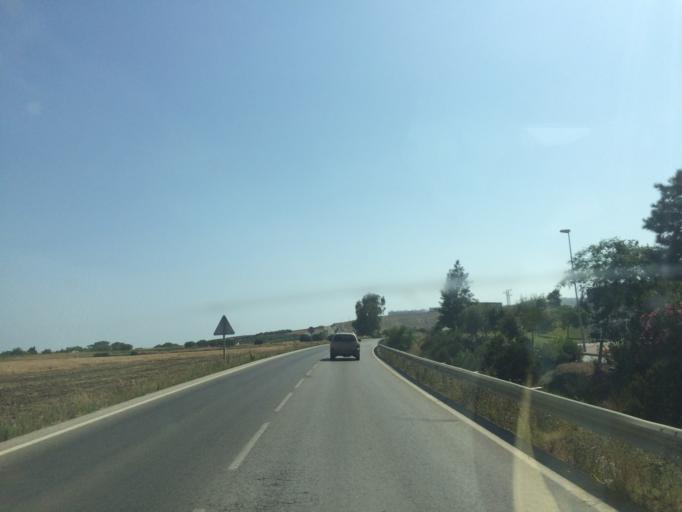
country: ES
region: Andalusia
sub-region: Provincia de Cadiz
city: Conil de la Frontera
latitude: 36.2884
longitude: -6.0662
